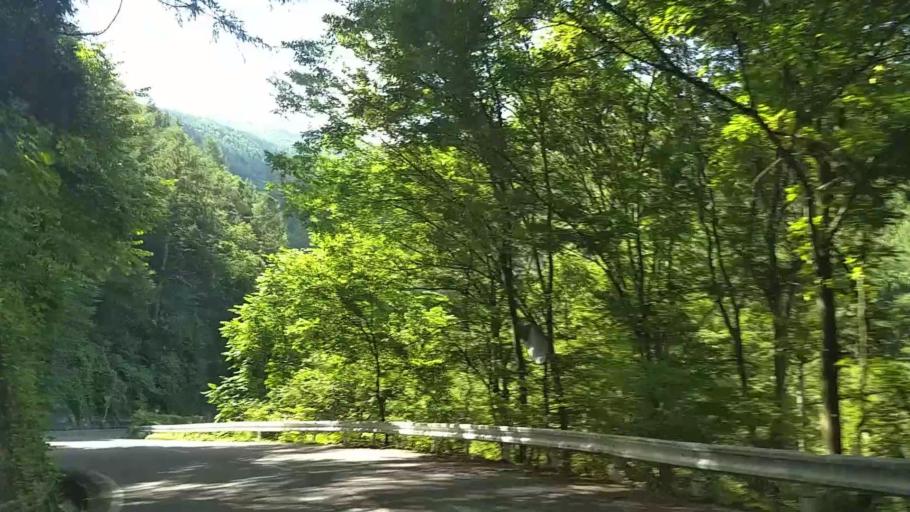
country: JP
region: Nagano
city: Matsumoto
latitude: 36.1977
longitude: 138.0653
